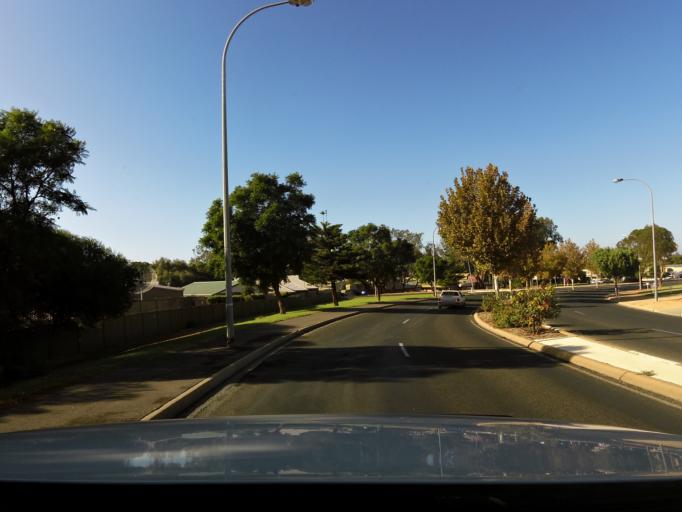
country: AU
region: South Australia
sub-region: Berri and Barmera
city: Berri
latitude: -34.2756
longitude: 140.6099
